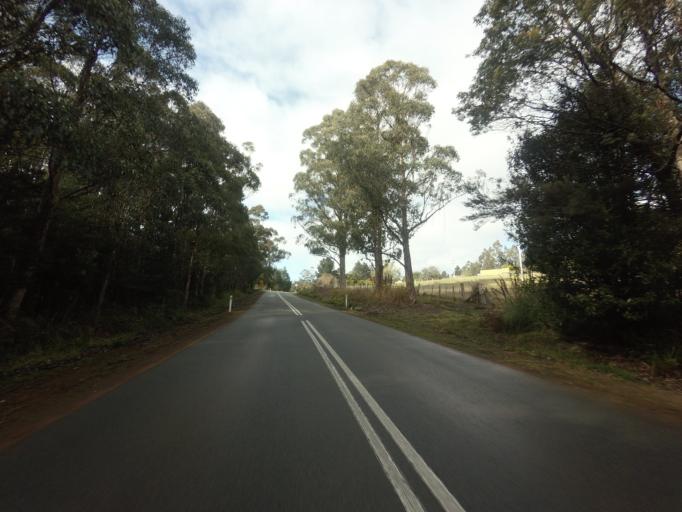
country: AU
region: Tasmania
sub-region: Huon Valley
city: Geeveston
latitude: -43.3582
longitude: 146.9591
